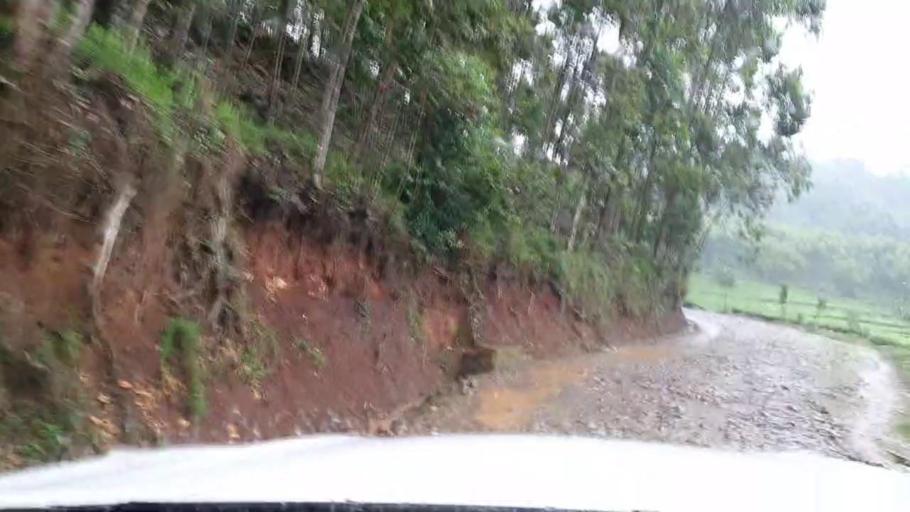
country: RW
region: Western Province
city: Cyangugu
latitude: -2.4651
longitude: 29.0346
